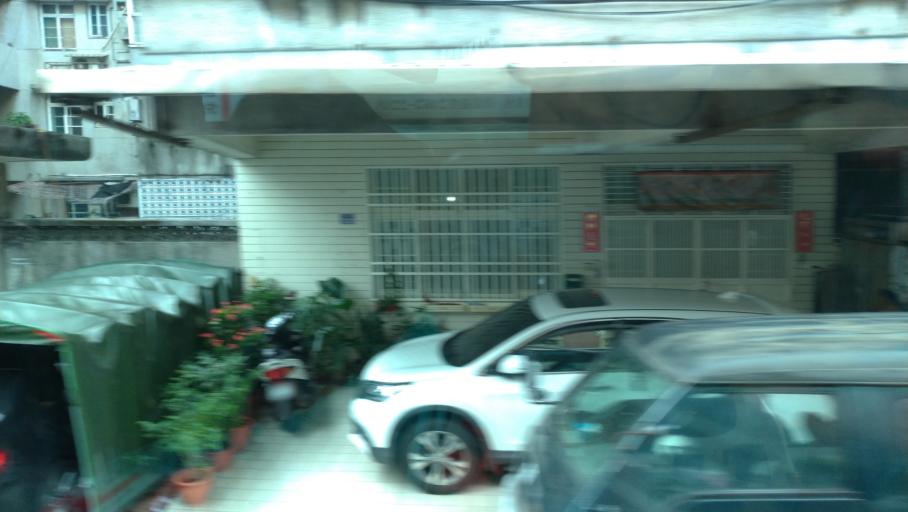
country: TW
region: Taiwan
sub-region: Keelung
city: Keelung
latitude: 25.1476
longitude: 121.7617
